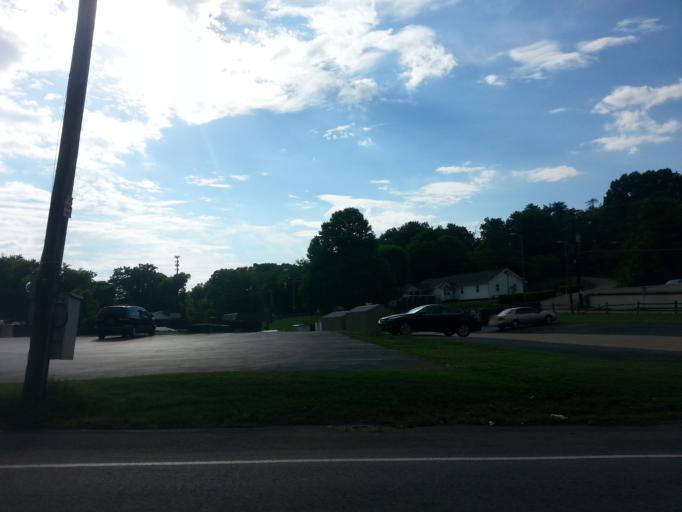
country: US
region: Tennessee
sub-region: Knox County
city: Knoxville
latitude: 35.9272
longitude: -83.9917
